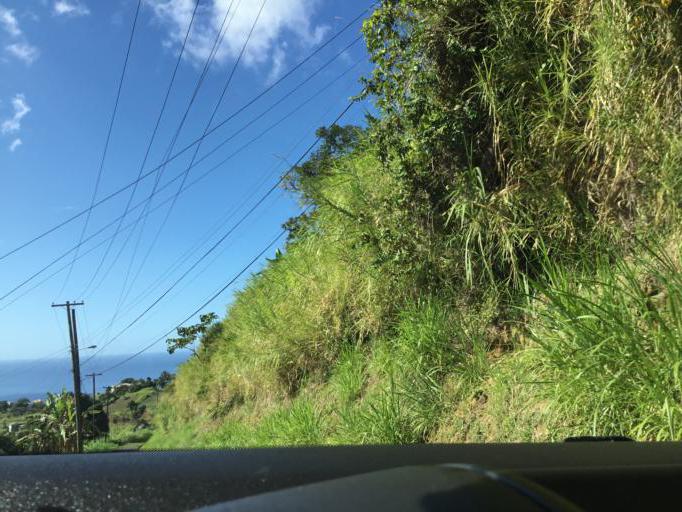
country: VC
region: Saint David
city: Chateaubelair
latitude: 13.2727
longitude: -61.2425
